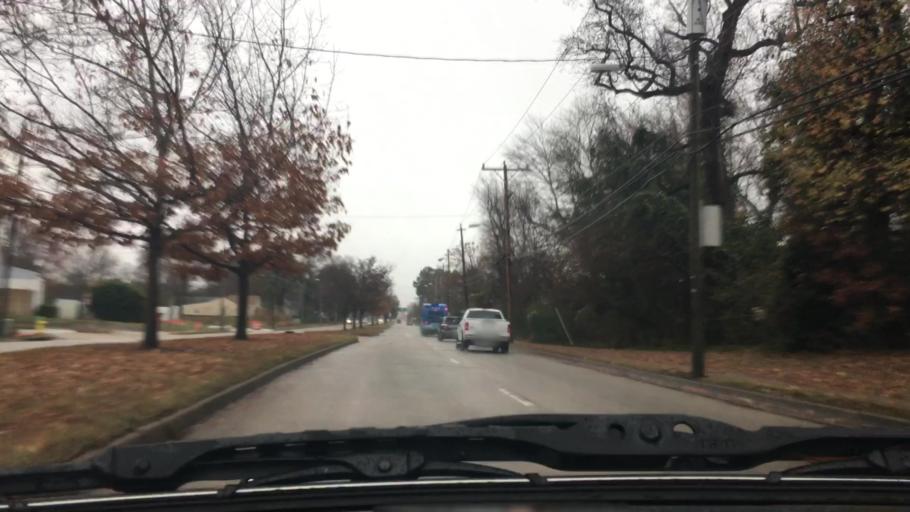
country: US
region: Virginia
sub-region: City of Norfolk
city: Norfolk
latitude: 36.9233
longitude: -76.2526
